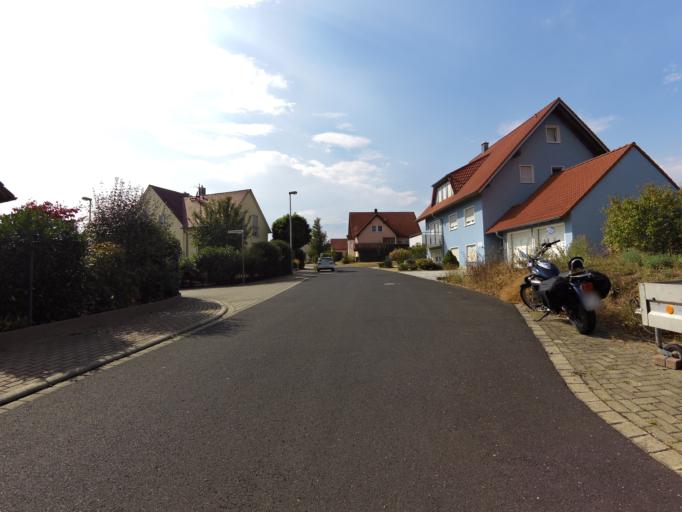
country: DE
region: Bavaria
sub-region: Regierungsbezirk Unterfranken
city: Hettstadt
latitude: 49.8051
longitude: 9.8230
